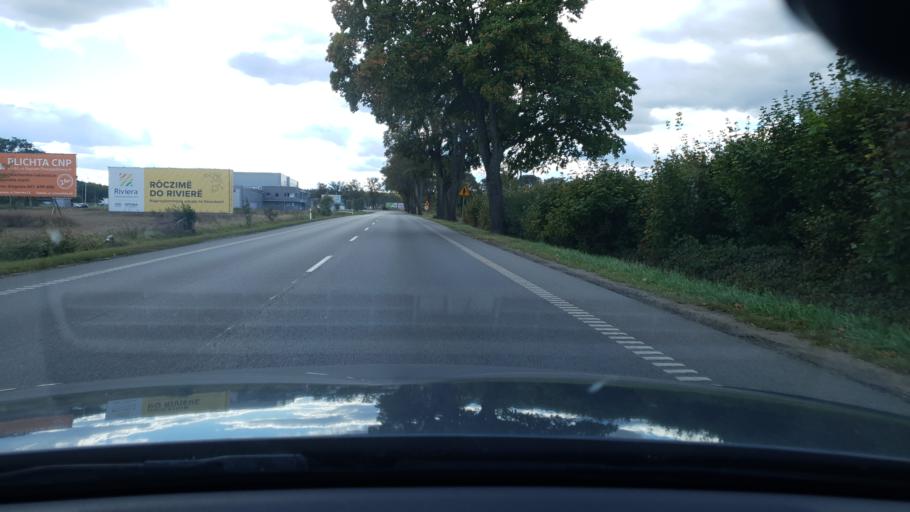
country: PL
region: Pomeranian Voivodeship
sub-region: Powiat wejherowski
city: Rekowo Dolne
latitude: 54.6435
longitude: 18.3495
